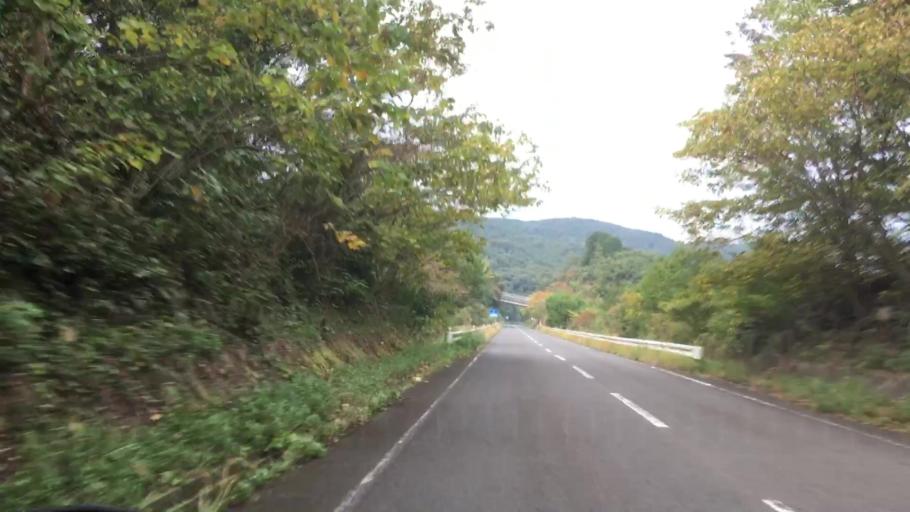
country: JP
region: Nagasaki
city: Sasebo
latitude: 32.9959
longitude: 129.7129
